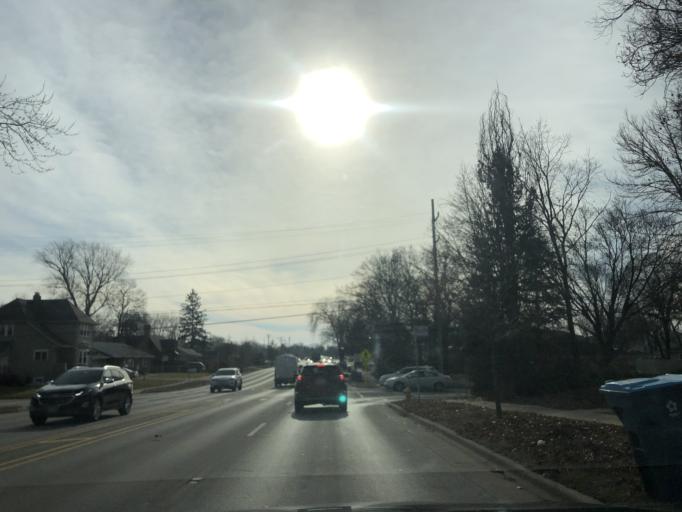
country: US
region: Illinois
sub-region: DuPage County
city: Downers Grove
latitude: 41.8116
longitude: -88.0112
